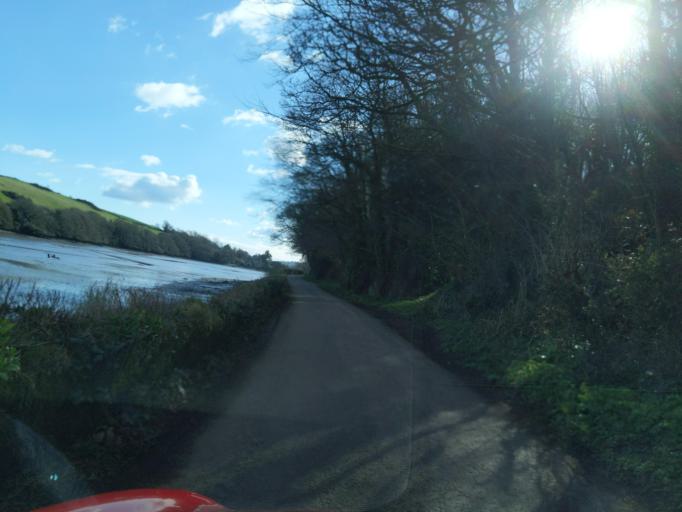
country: GB
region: England
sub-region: Devon
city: Kingsbridge
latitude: 50.2813
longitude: -3.7597
